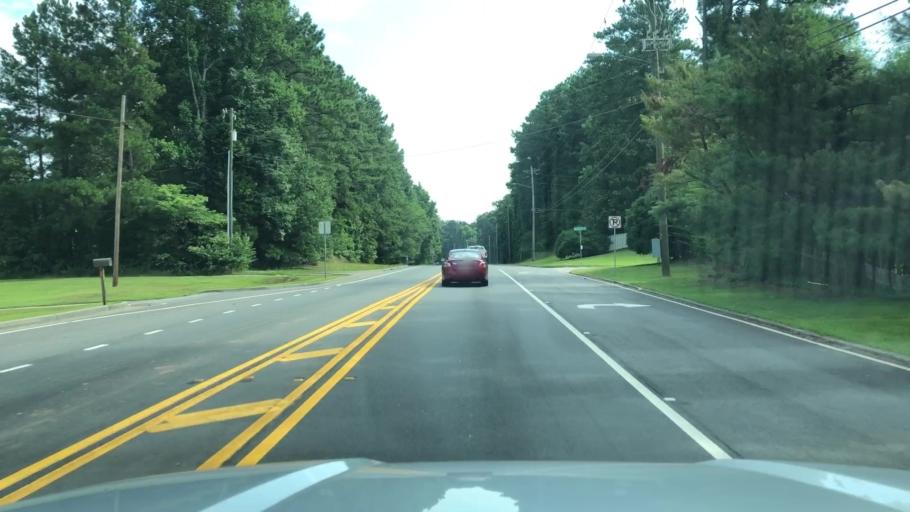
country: US
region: Georgia
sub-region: Cobb County
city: Acworth
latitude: 34.0471
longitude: -84.7270
